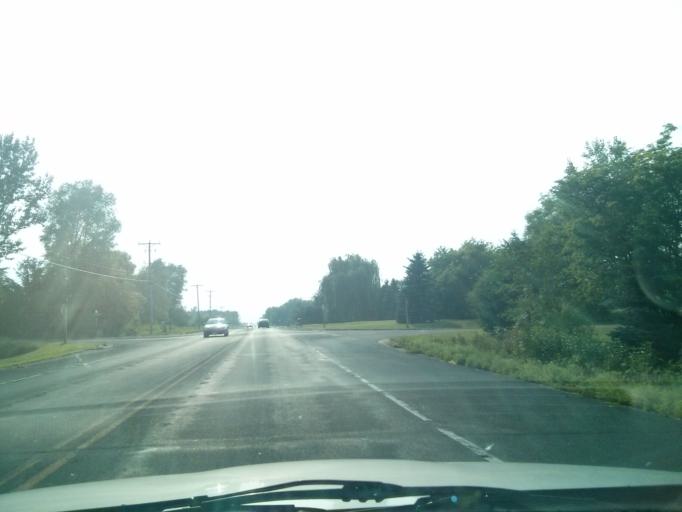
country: US
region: Wisconsin
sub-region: Saint Croix County
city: Hudson
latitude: 44.9781
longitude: -92.6886
